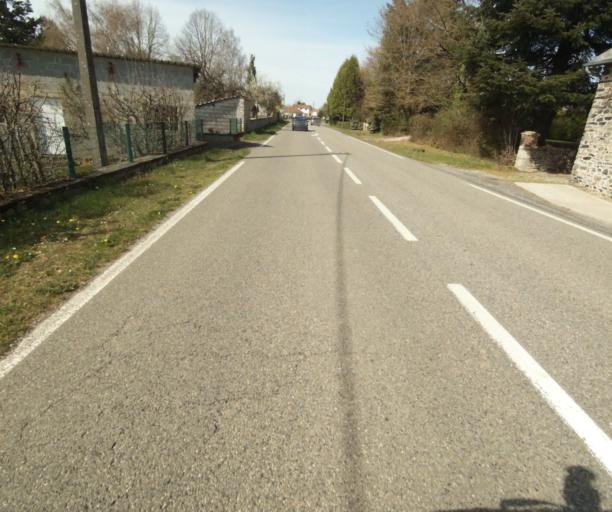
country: FR
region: Limousin
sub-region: Departement de la Correze
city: Seilhac
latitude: 45.3632
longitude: 1.7251
